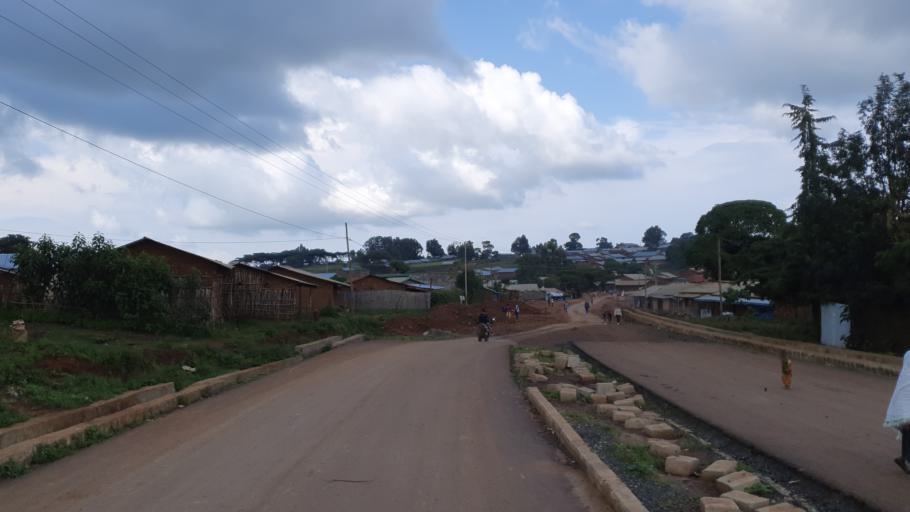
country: ET
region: Amhara
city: Bure
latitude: 10.1419
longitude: 36.9308
